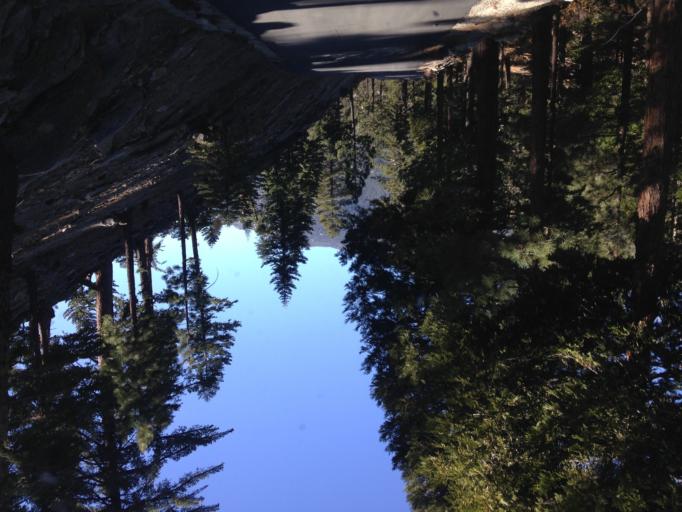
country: US
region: California
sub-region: Riverside County
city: Idyllwild-Pine Cove
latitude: 33.8238
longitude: -116.7514
